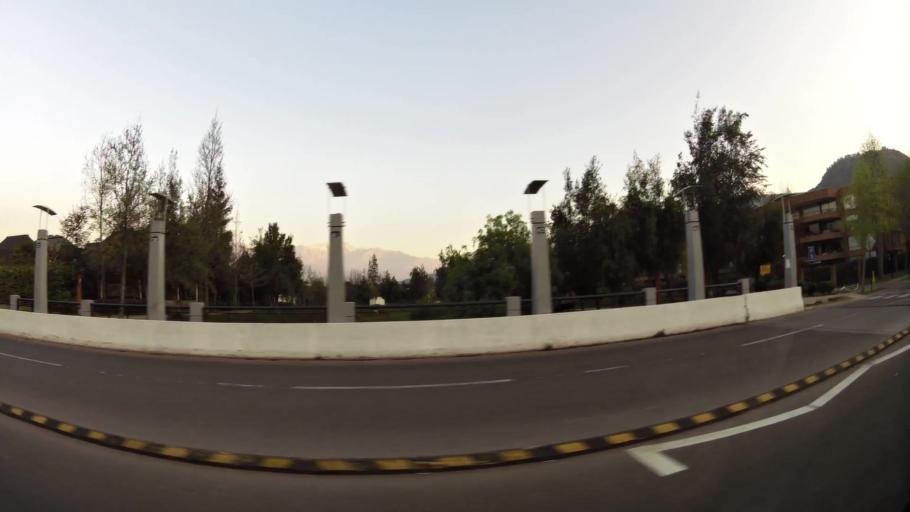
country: CL
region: Santiago Metropolitan
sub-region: Provincia de Chacabuco
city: Chicureo Abajo
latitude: -33.3371
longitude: -70.5511
